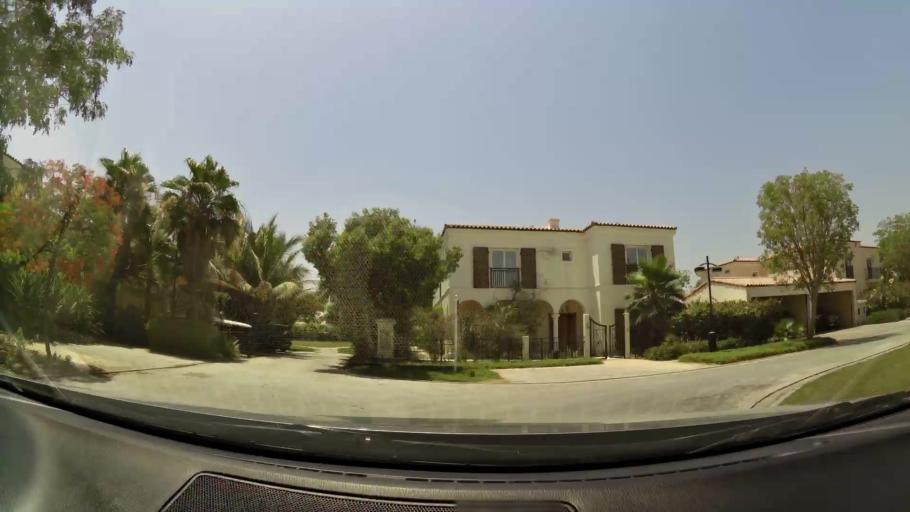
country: AE
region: Dubai
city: Dubai
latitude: 24.9958
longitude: 55.1663
